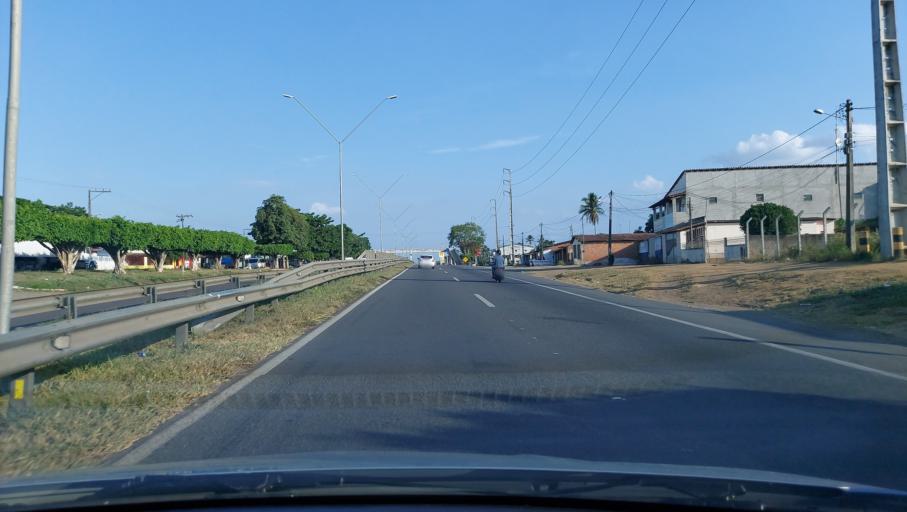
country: BR
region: Bahia
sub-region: Conceicao Do Jacuipe
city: Conceicao do Jacuipe
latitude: -12.3669
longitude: -38.8166
